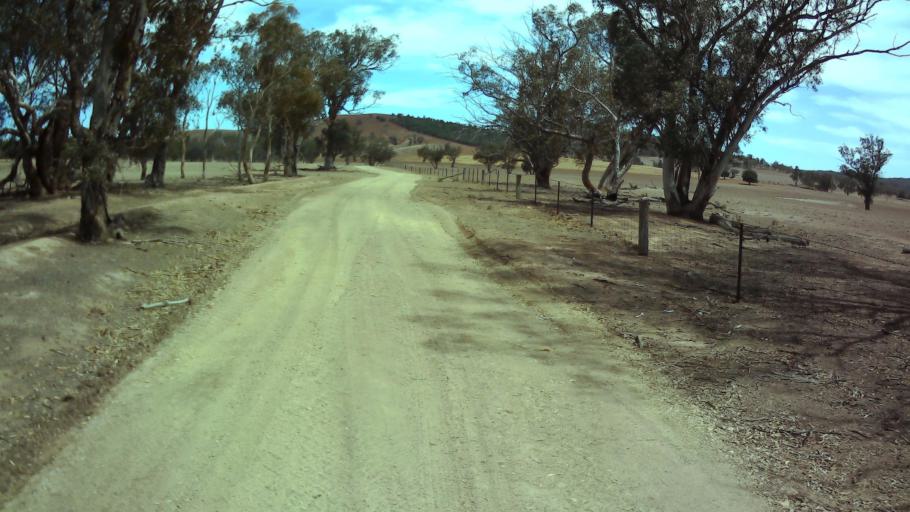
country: AU
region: New South Wales
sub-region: Weddin
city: Grenfell
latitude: -33.7806
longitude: 148.1513
